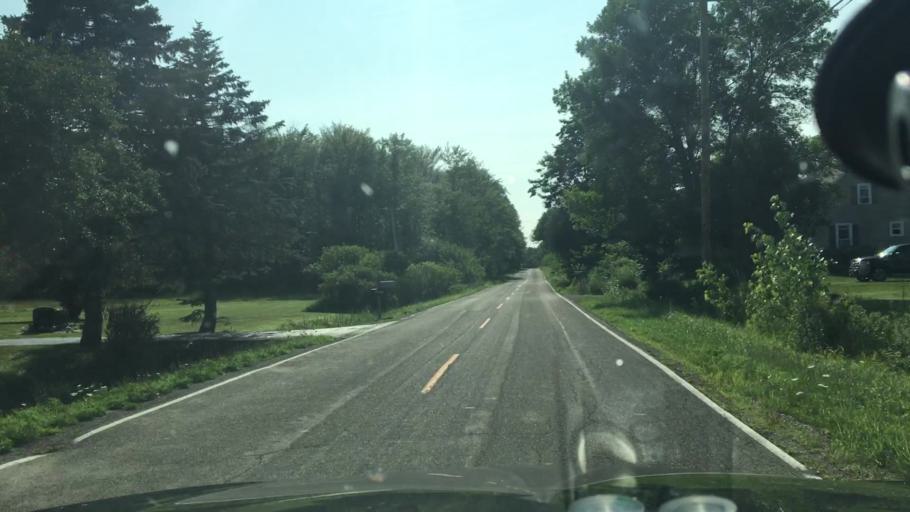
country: US
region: New York
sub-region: Erie County
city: North Collins
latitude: 42.6197
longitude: -78.9394
